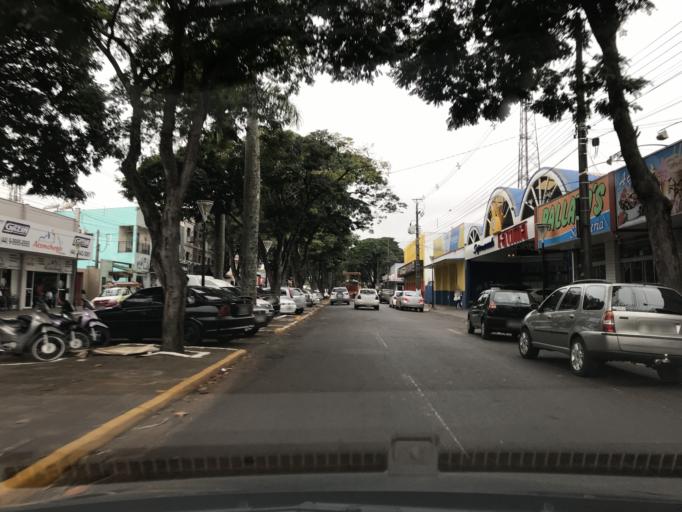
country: PY
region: Canindeyu
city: Salto del Guaira
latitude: -24.0829
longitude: -54.2471
